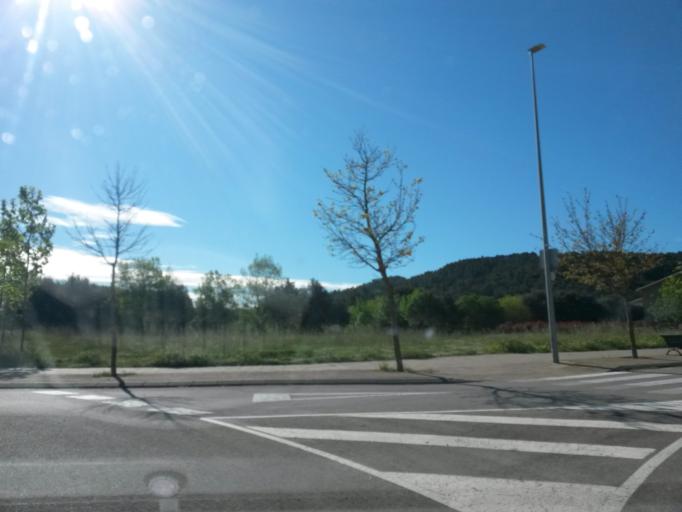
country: ES
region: Catalonia
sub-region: Provincia de Girona
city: Celra
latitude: 42.0262
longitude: 2.8914
